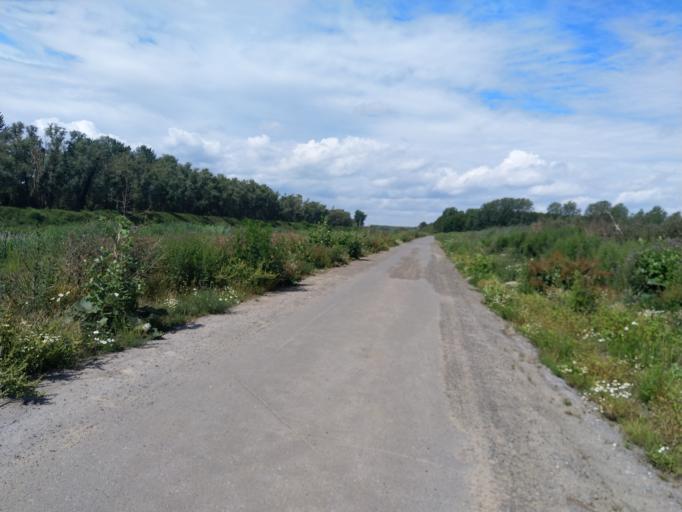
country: BE
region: Wallonia
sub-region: Province du Hainaut
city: Bernissart
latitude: 50.4503
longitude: 3.6407
